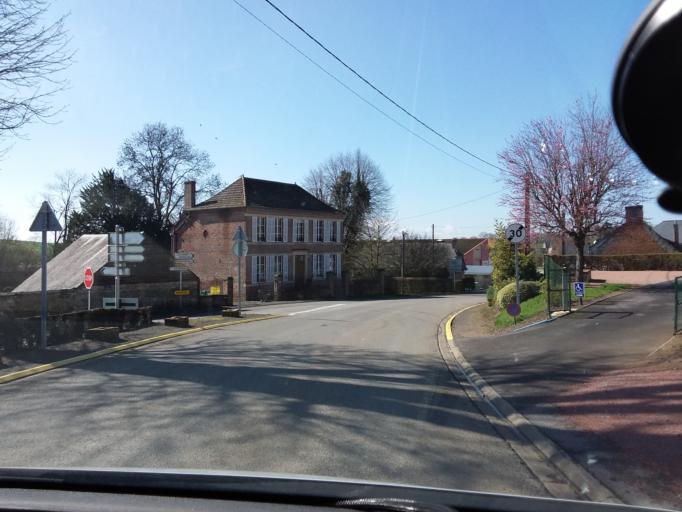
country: FR
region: Picardie
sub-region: Departement de l'Aisne
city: Montcornet
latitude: 49.7398
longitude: 3.9916
